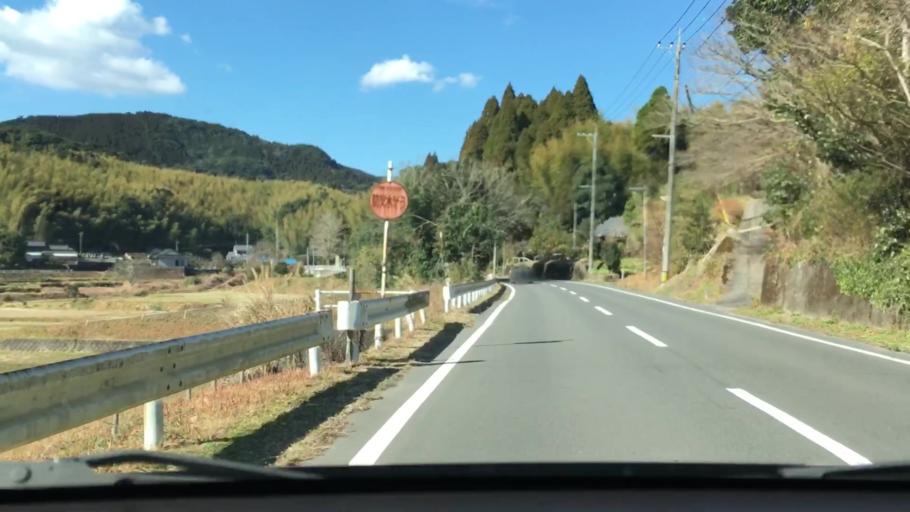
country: JP
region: Kagoshima
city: Ijuin
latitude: 31.7062
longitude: 130.4450
